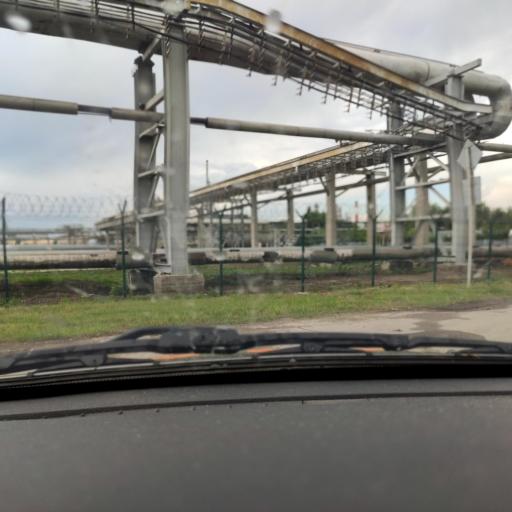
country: RU
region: Samara
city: Tol'yatti
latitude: 53.5342
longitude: 49.4694
